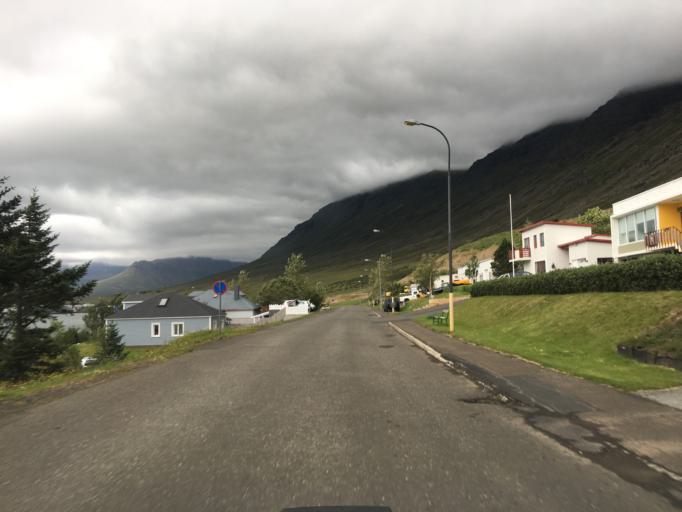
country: IS
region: East
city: Neskaupstadur
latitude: 65.1483
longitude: -13.7094
